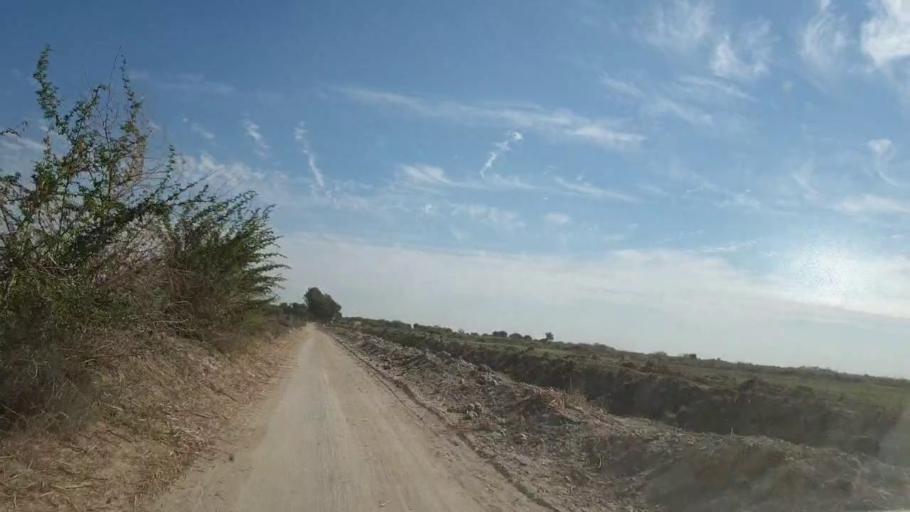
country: PK
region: Sindh
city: Pithoro
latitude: 25.5413
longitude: 69.3010
